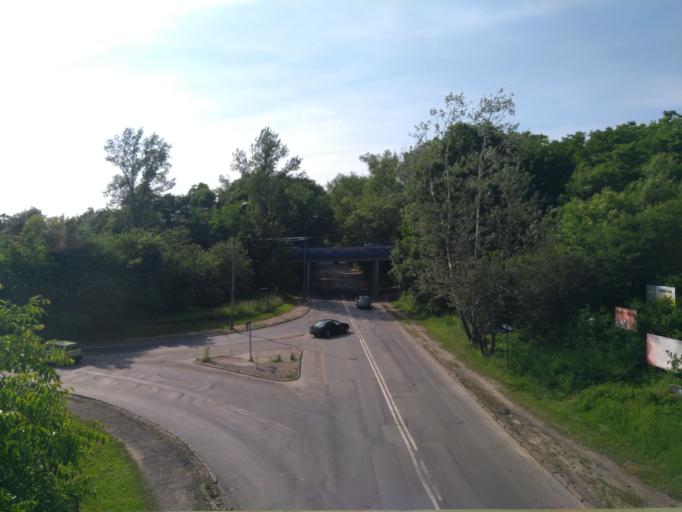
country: PL
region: Lesser Poland Voivodeship
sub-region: Powiat wielicki
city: Kokotow
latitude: 50.0888
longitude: 20.0572
